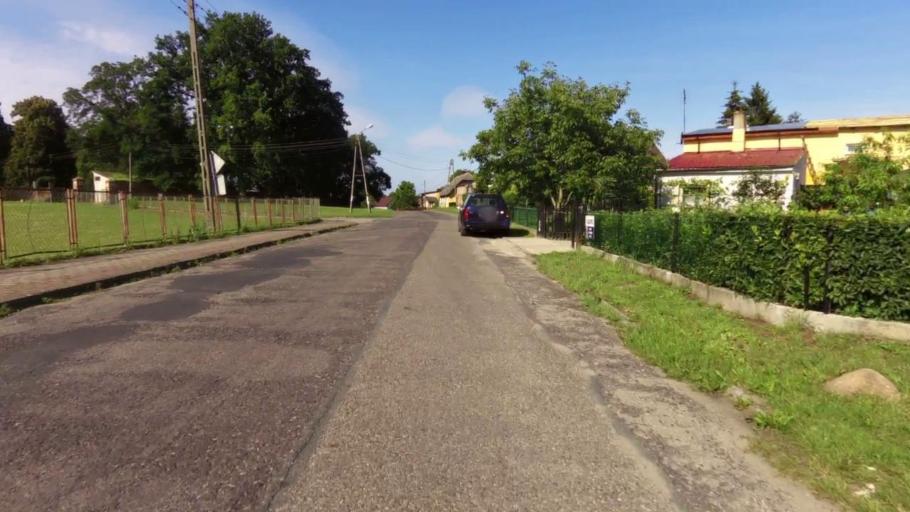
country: PL
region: West Pomeranian Voivodeship
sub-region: Powiat stargardzki
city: Marianowo
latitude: 53.3804
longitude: 15.2663
